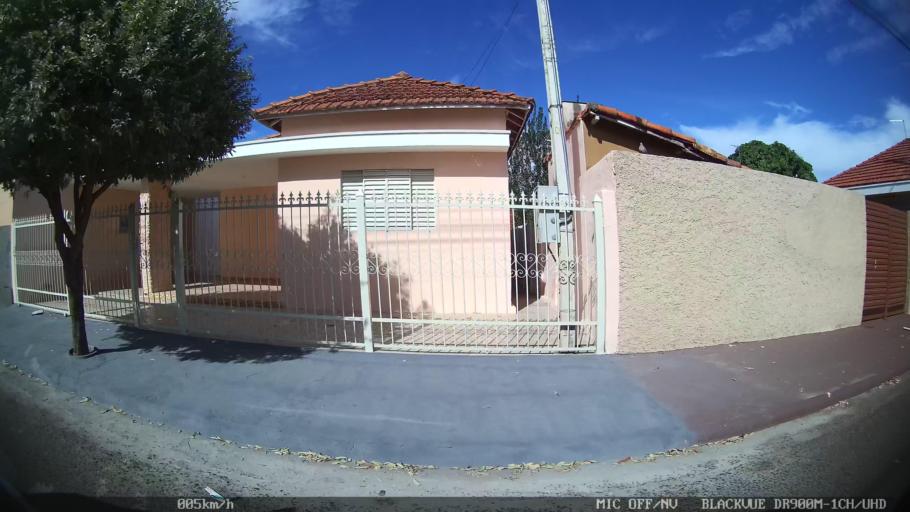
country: BR
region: Sao Paulo
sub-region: Catanduva
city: Catanduva
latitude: -21.1266
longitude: -48.9701
